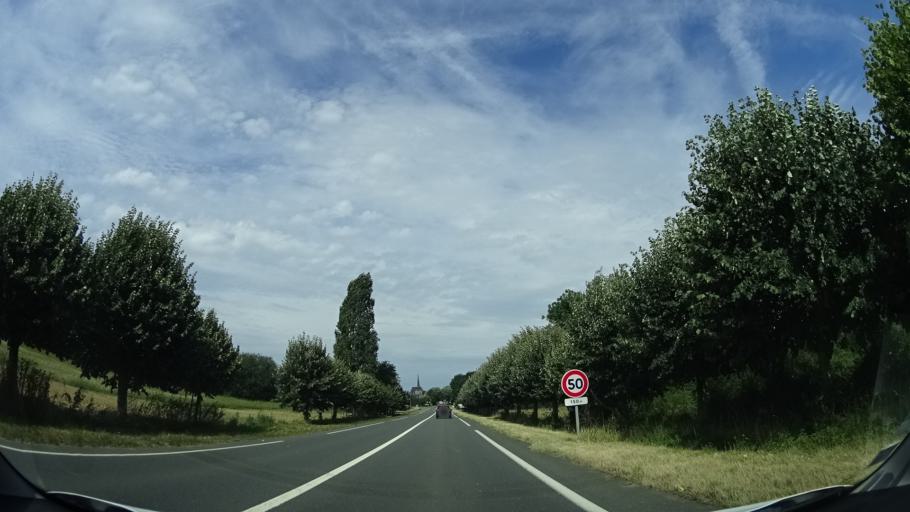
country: FR
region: Pays de la Loire
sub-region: Departement de la Sarthe
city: Bazouges-sur-le-Loir
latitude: 47.7442
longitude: -0.1444
